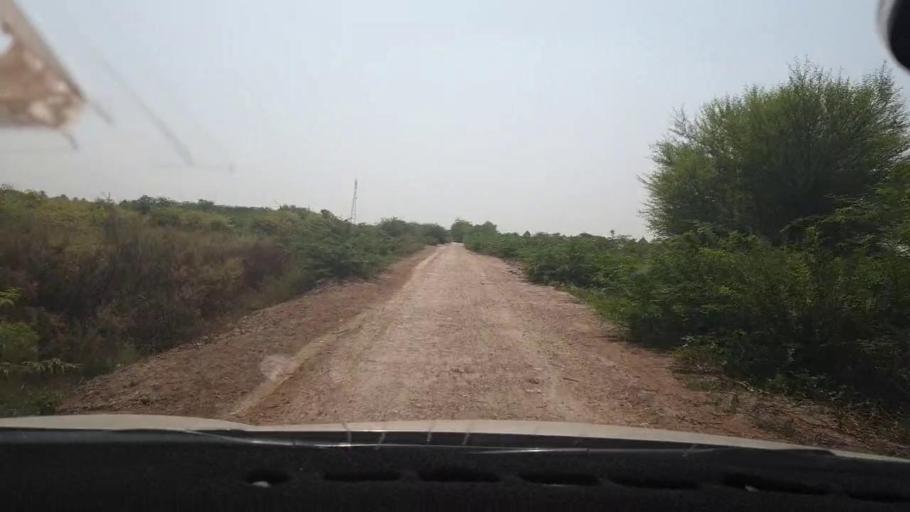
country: PK
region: Sindh
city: Tando Mittha Khan
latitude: 25.9242
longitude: 69.2248
